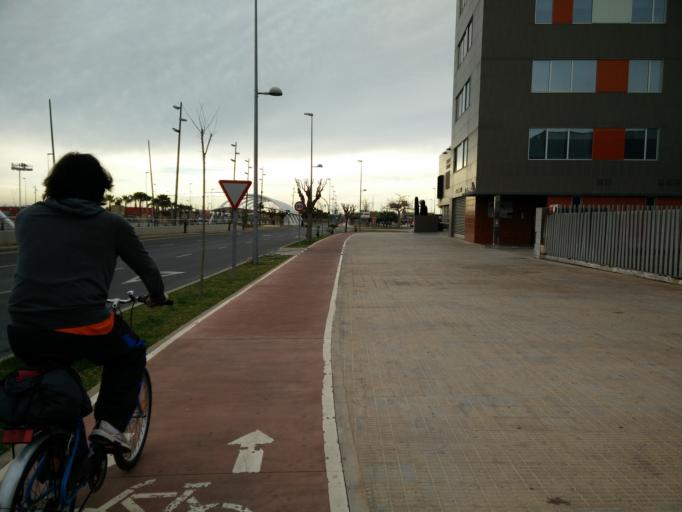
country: ES
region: Valencia
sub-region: Provincia de Castello
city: Castello de la Plana
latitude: 39.9835
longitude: -0.0243
